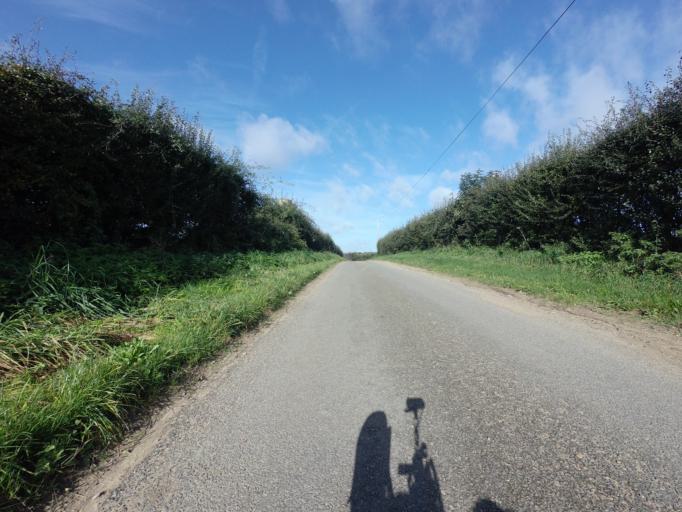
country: GB
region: England
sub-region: Norfolk
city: Dersingham
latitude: 52.8533
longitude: 0.6660
